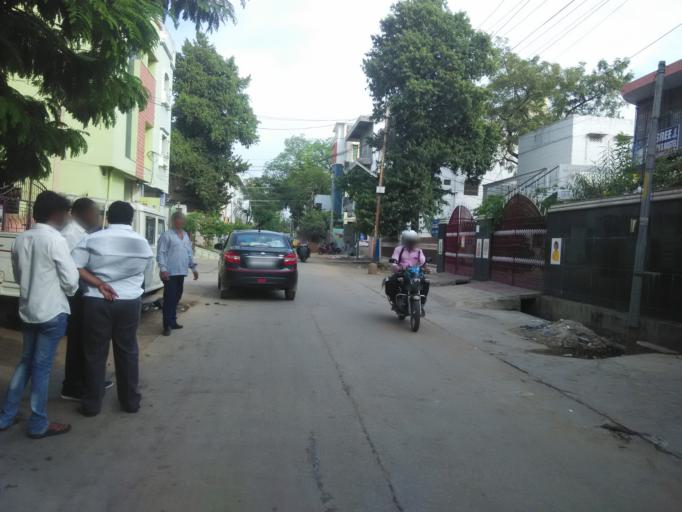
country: IN
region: Andhra Pradesh
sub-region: Kurnool
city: Nandyal
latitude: 15.4868
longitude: 78.4789
